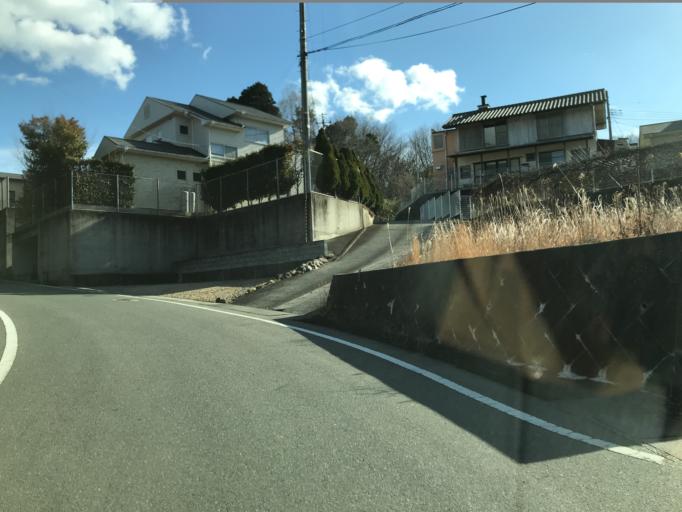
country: JP
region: Fukushima
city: Iwaki
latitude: 37.1258
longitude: 140.8420
